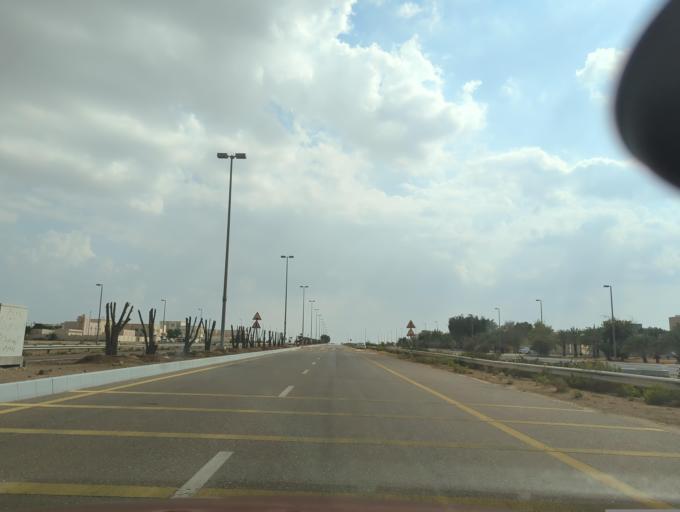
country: AE
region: Abu Dhabi
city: Abu Dhabi
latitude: 24.3718
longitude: 54.7177
